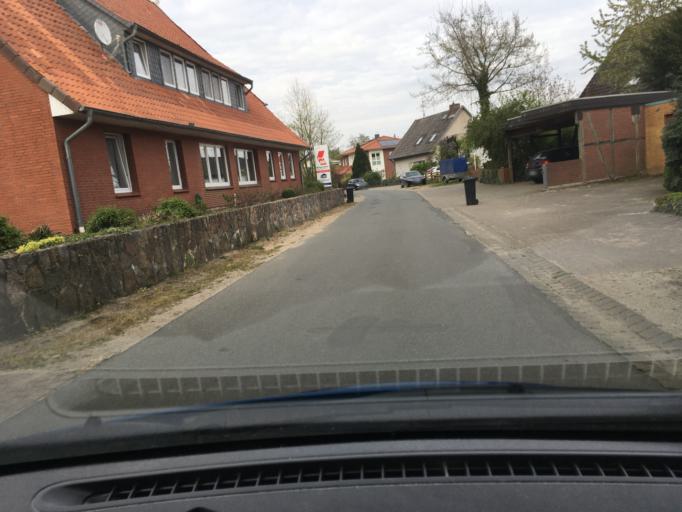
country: DE
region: Lower Saxony
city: Neetze
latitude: 53.2637
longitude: 10.6145
